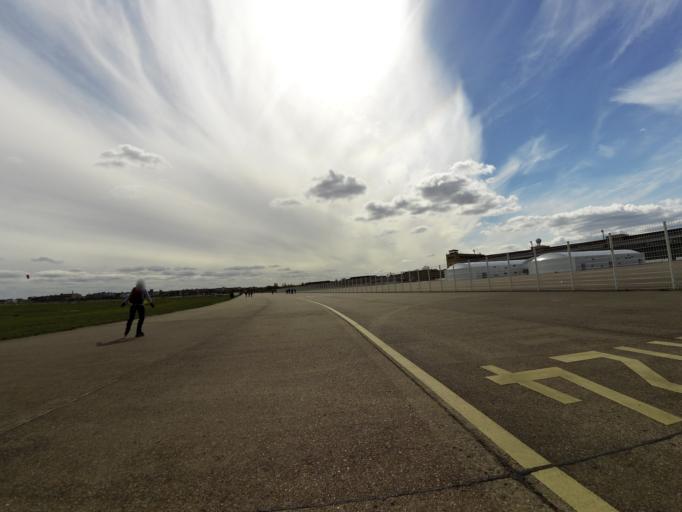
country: DE
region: Berlin
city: Tempelhof Bezirk
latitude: 52.4792
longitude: 13.3928
